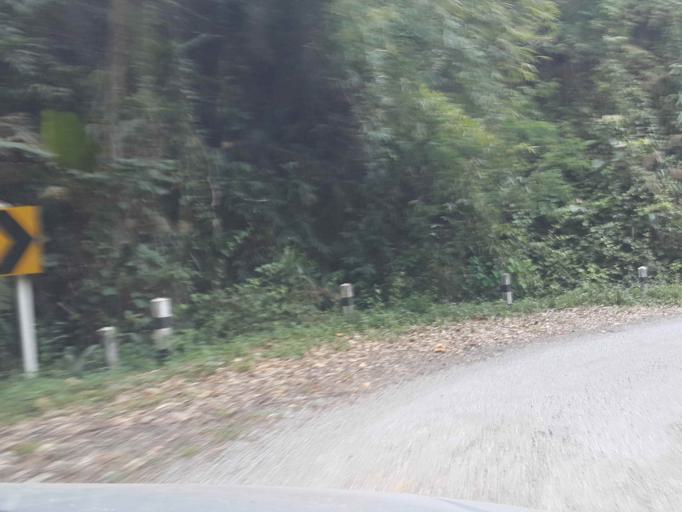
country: TH
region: Chiang Mai
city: Mae On
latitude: 18.9565
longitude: 99.3369
